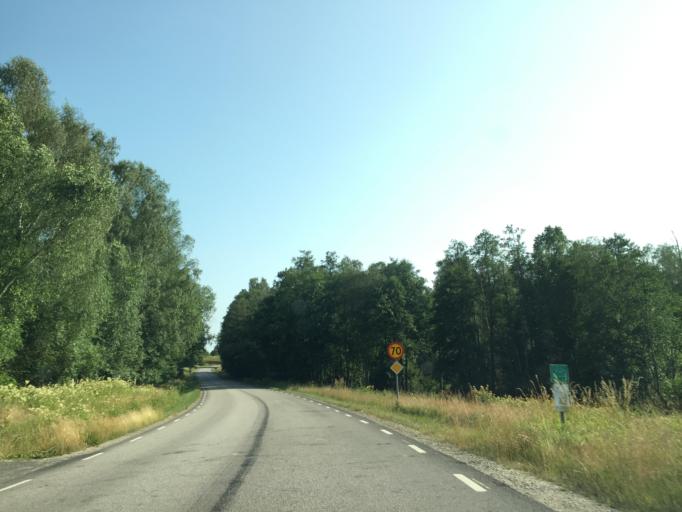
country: SE
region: Vaestra Goetaland
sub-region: Trollhattan
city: Trollhattan
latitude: 58.2860
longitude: 12.2493
